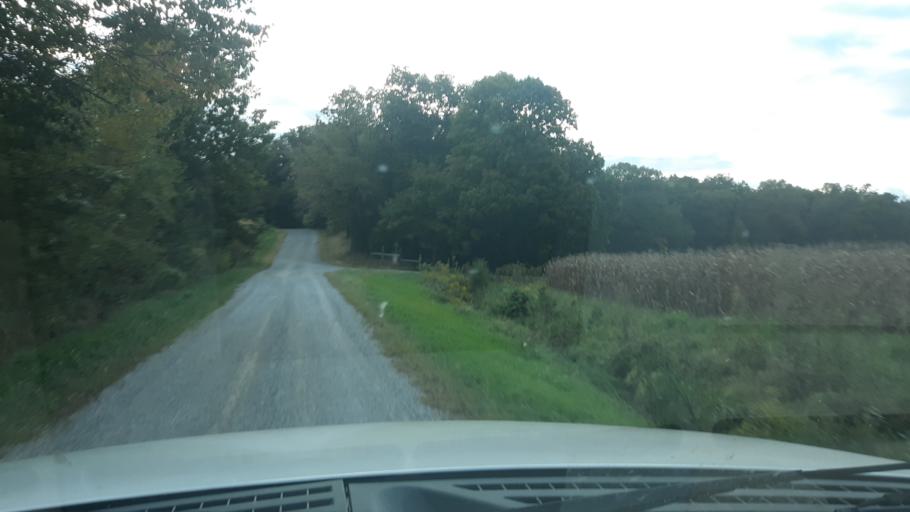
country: US
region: Illinois
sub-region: Saline County
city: Eldorado
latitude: 37.8374
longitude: -88.4800
